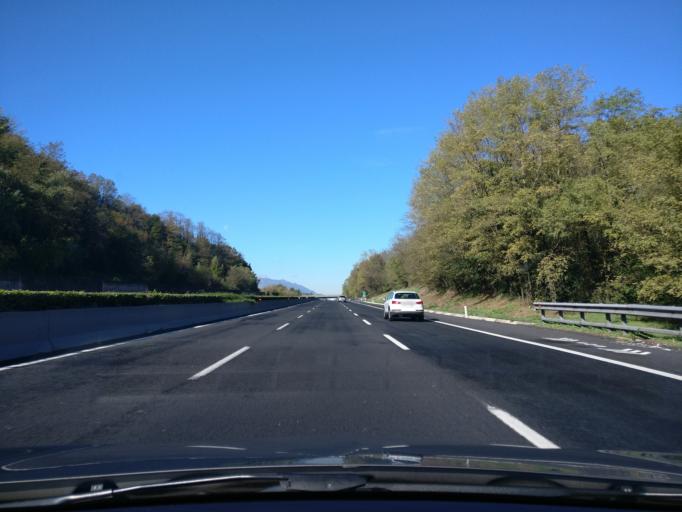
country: IT
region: Latium
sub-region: Provincia di Frosinone
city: Pofi
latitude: 41.5624
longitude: 13.4024
